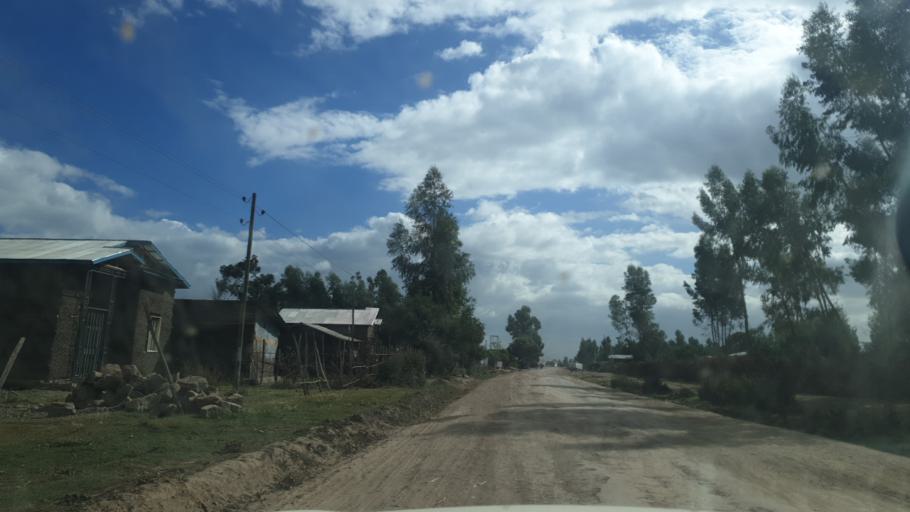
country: ET
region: Oromiya
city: Ziway
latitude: 7.7356
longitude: 39.0333
